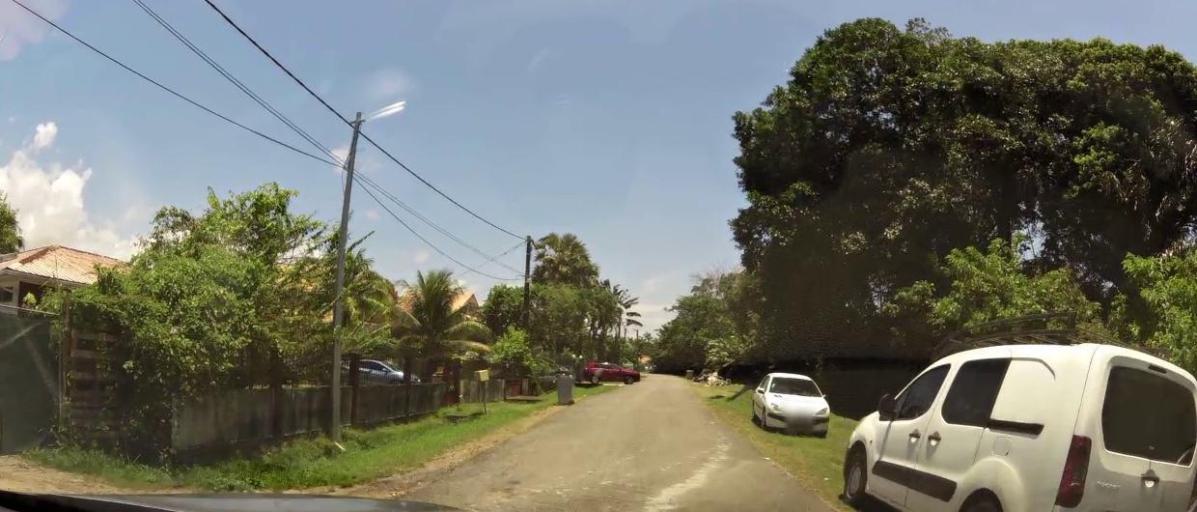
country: GF
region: Guyane
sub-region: Guyane
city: Cayenne
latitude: 4.9364
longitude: -52.3054
